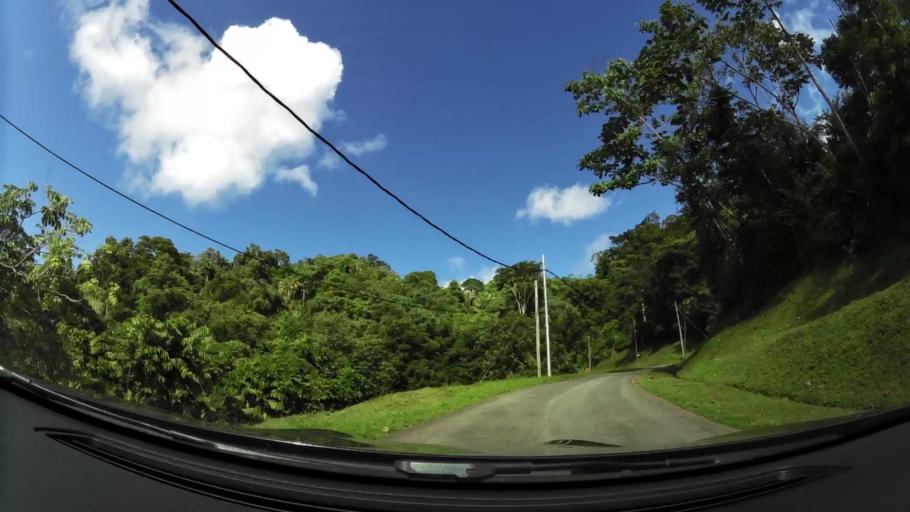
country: TT
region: Eastern Tobago
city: Roxborough
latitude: 11.3068
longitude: -60.6282
